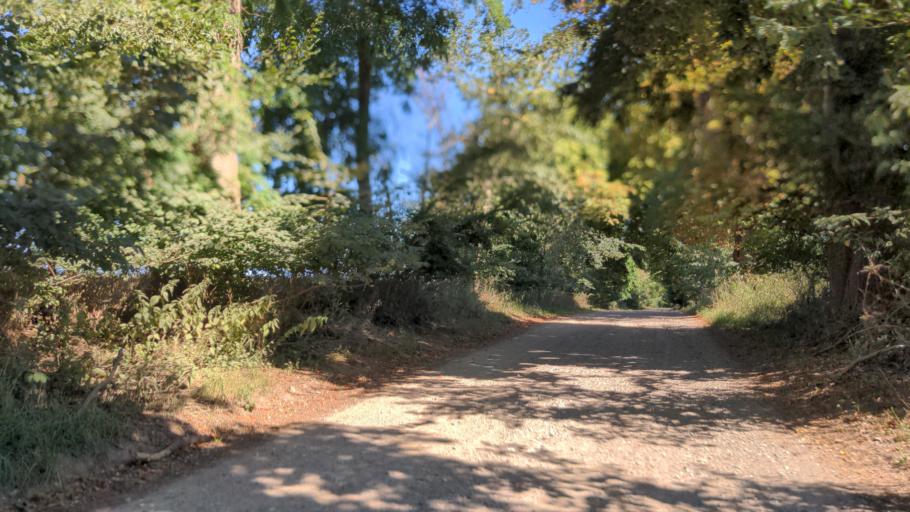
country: DE
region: Mecklenburg-Vorpommern
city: Klutz
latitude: 53.9805
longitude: 11.1713
